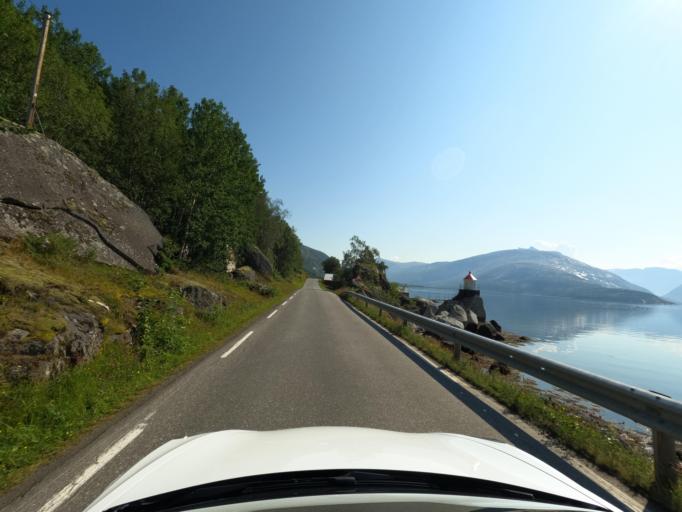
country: NO
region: Nordland
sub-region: Narvik
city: Narvik
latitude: 68.2846
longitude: 17.3733
